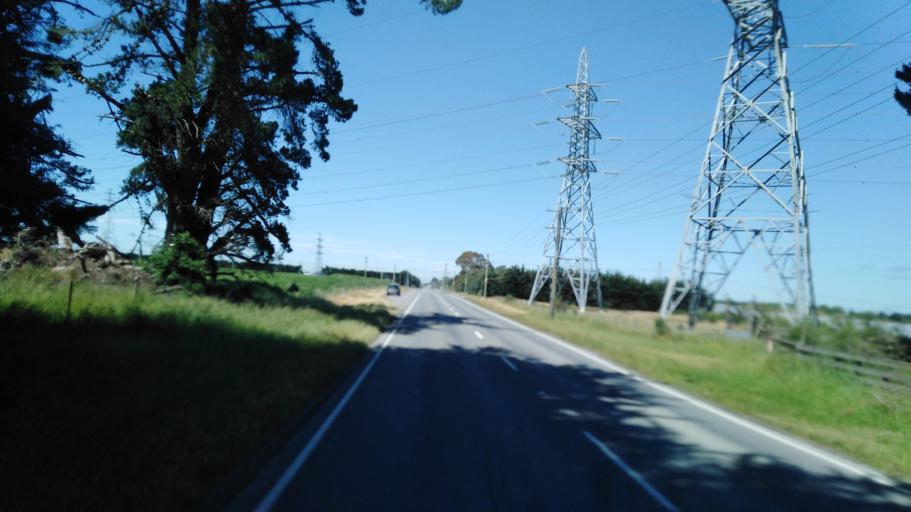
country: NZ
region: Canterbury
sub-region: Selwyn District
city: Prebbleton
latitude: -43.5250
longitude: 172.5016
